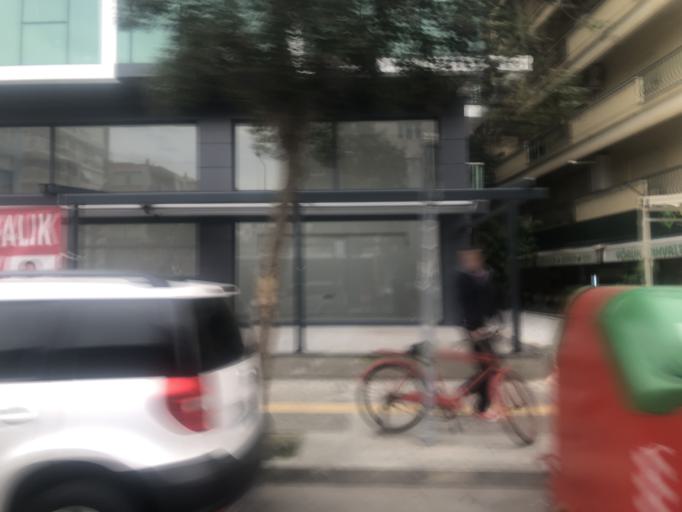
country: TR
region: Izmir
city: Karsiyaka
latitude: 38.4549
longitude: 27.1066
